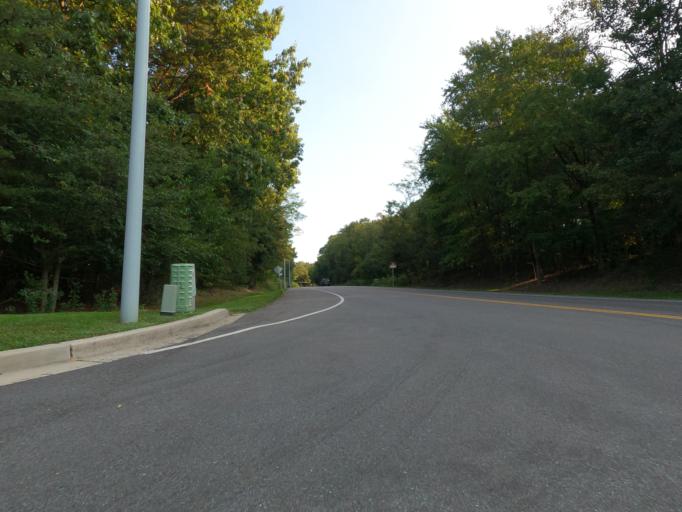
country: US
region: Maryland
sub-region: Anne Arundel County
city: South Gate
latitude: 39.1032
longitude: -76.6076
